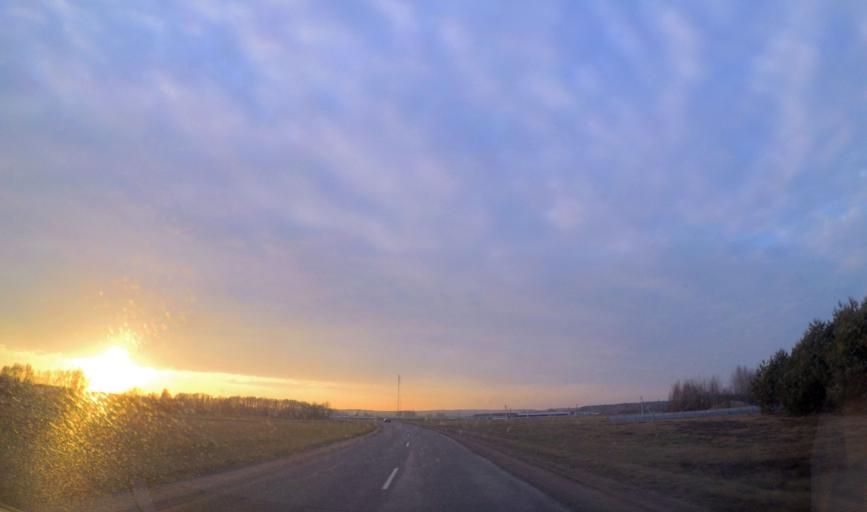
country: BY
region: Grodnenskaya
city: Hrodna
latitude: 53.7631
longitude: 23.9450
